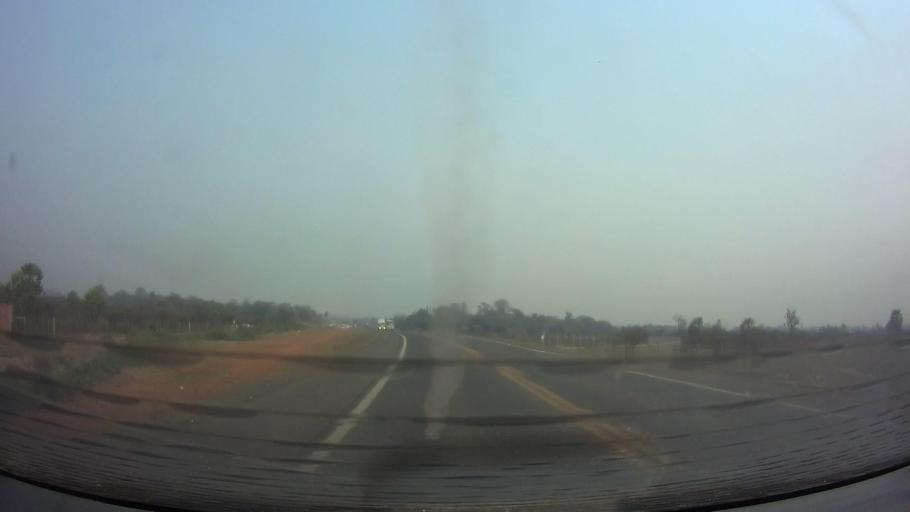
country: PY
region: Central
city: Limpio
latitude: -25.1546
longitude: -57.4871
